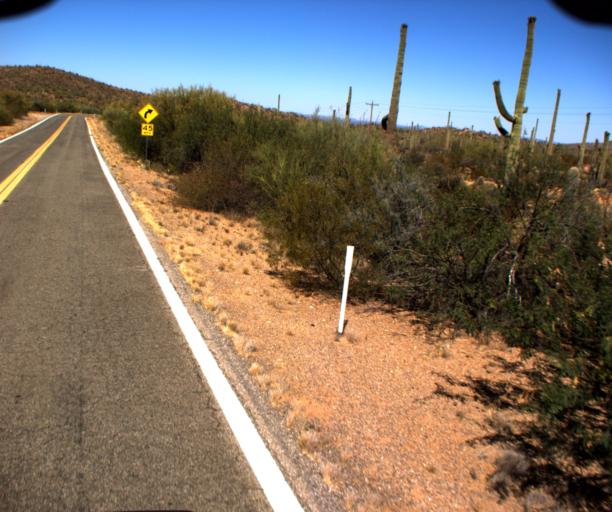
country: US
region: Arizona
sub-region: Pima County
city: Sells
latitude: 32.1734
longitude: -112.2036
